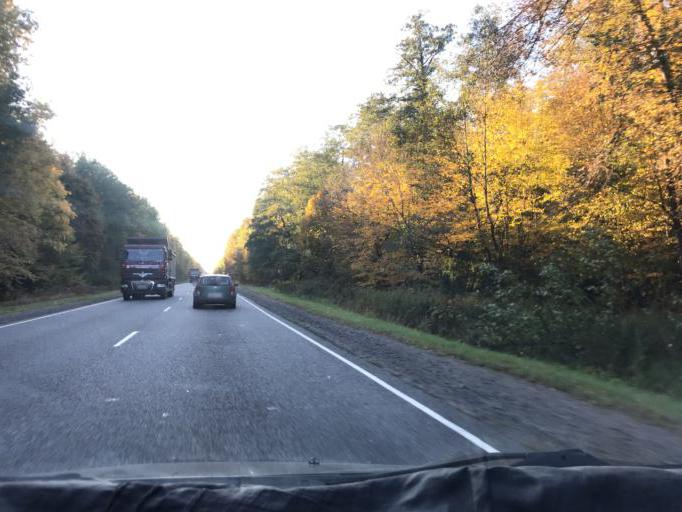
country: BY
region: Gomel
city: Zhytkavichy
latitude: 52.2732
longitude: 28.1030
